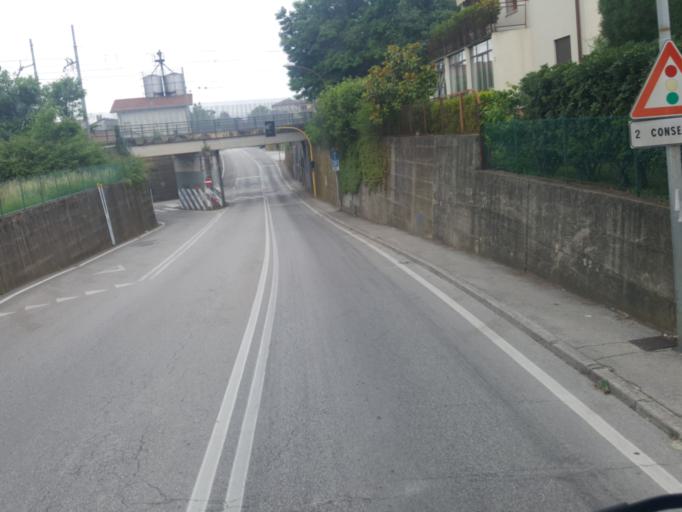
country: IT
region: Veneto
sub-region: Provincia di Vicenza
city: Bassano del Grappa
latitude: 45.7588
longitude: 11.7463
